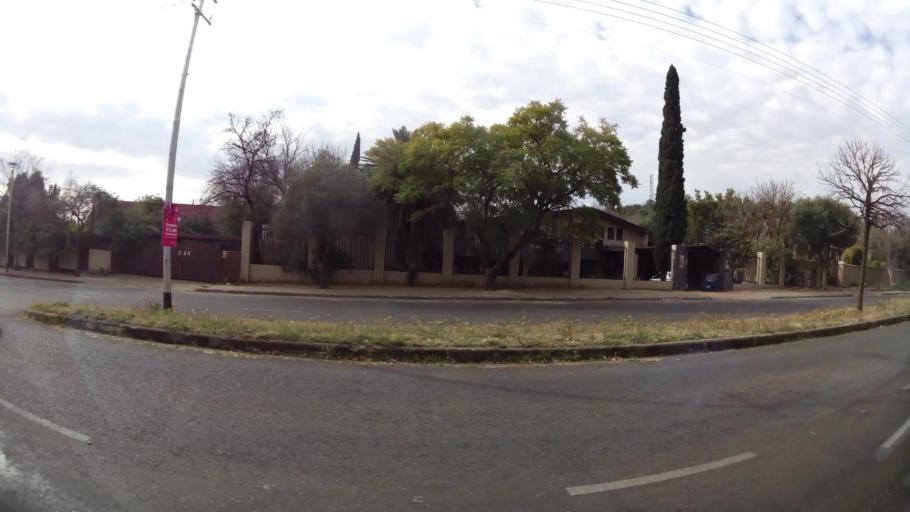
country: ZA
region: Orange Free State
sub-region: Mangaung Metropolitan Municipality
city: Bloemfontein
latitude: -29.0983
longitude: 26.2160
